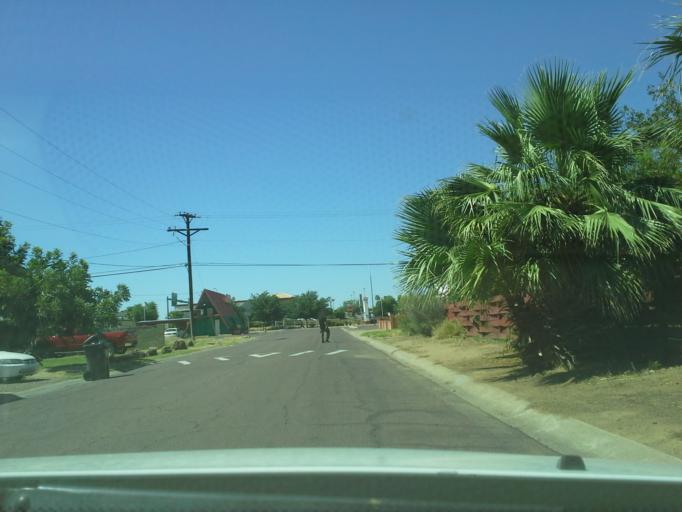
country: US
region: Arizona
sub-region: Maricopa County
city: Glendale
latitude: 33.5230
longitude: -112.1106
